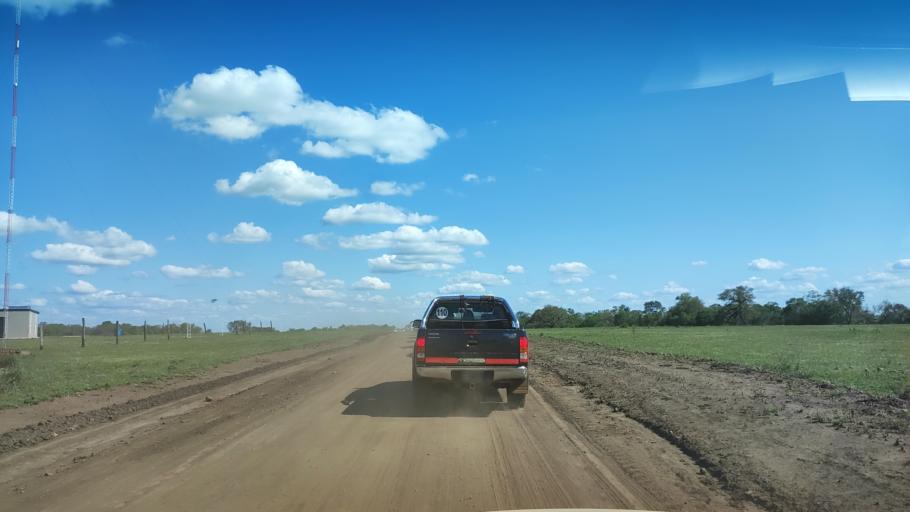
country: PY
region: Itapua
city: Carmen del Parana
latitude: -27.4150
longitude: -56.1719
